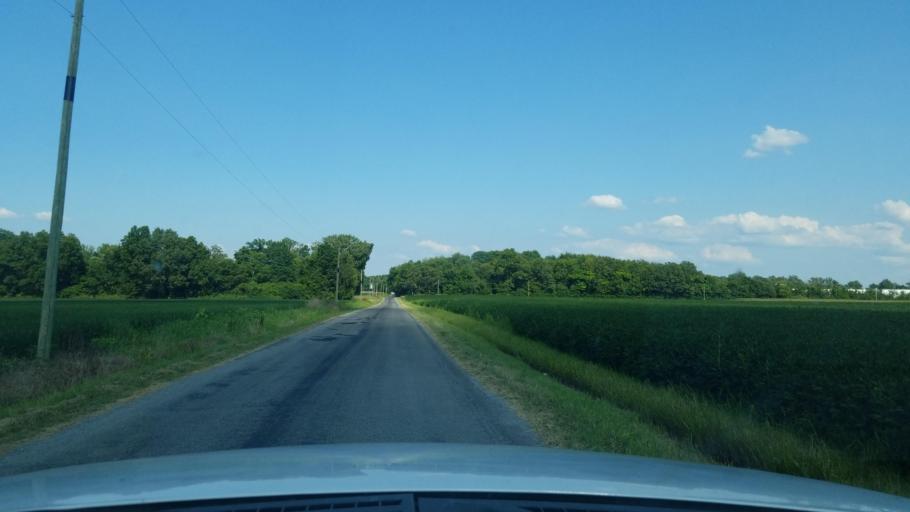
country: US
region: Illinois
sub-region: Saline County
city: Eldorado
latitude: 37.8050
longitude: -88.4700
